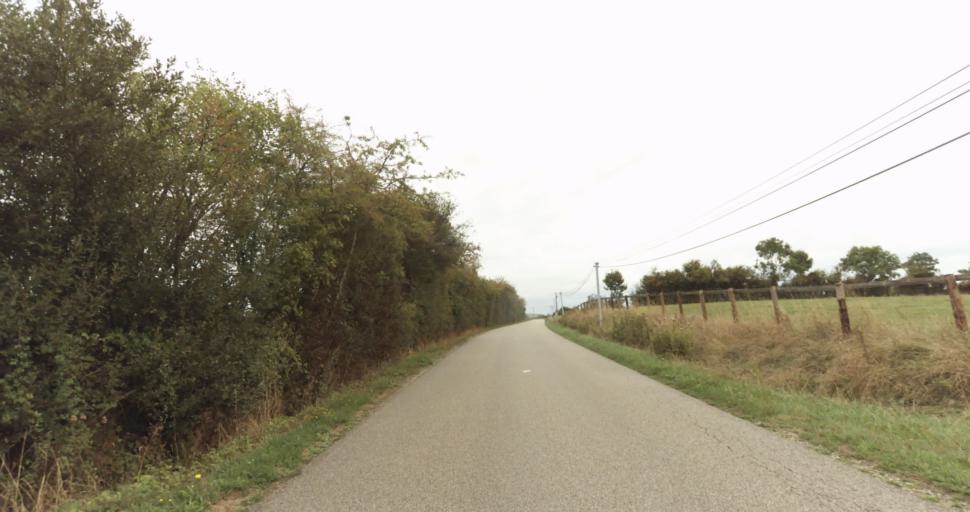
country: FR
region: Lower Normandy
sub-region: Departement de l'Orne
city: Sees
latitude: 48.6751
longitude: 0.2367
